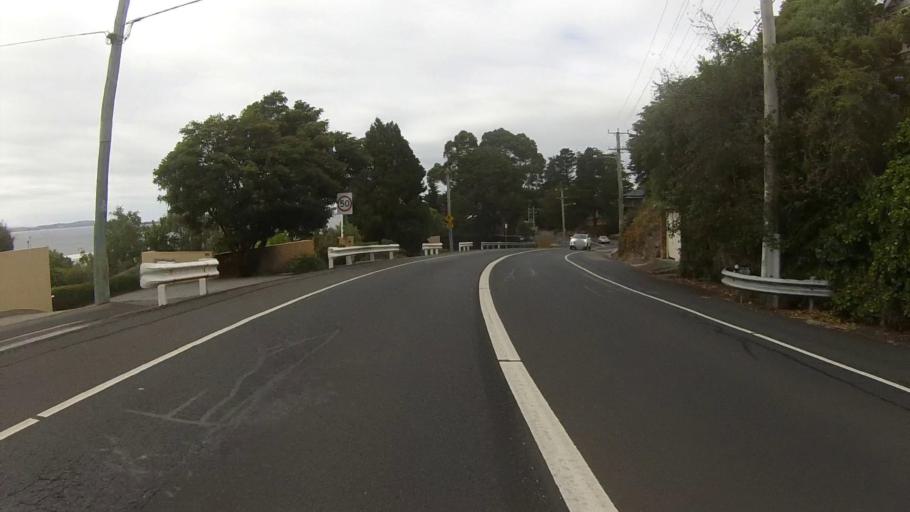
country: AU
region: Tasmania
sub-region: Kingborough
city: Taroona
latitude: -42.9255
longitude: 147.3607
